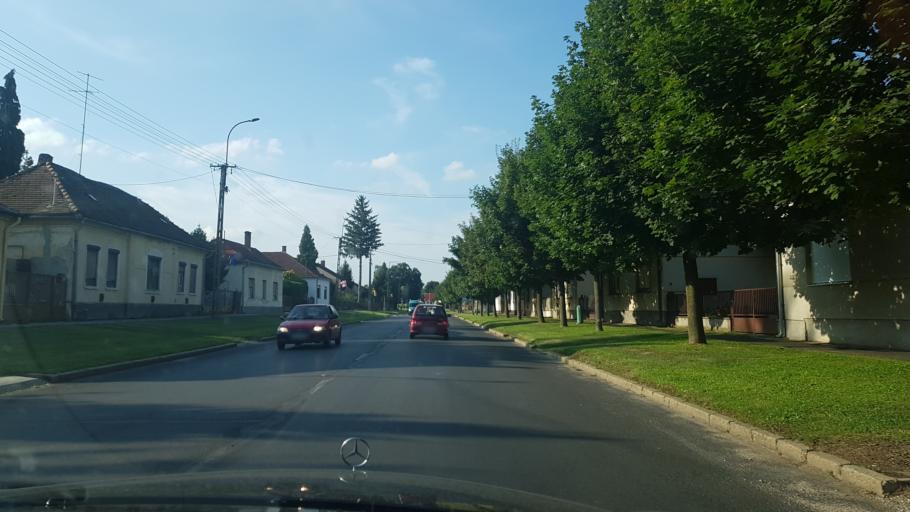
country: HU
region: Somogy
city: Nagyatad
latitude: 46.2359
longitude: 17.3569
